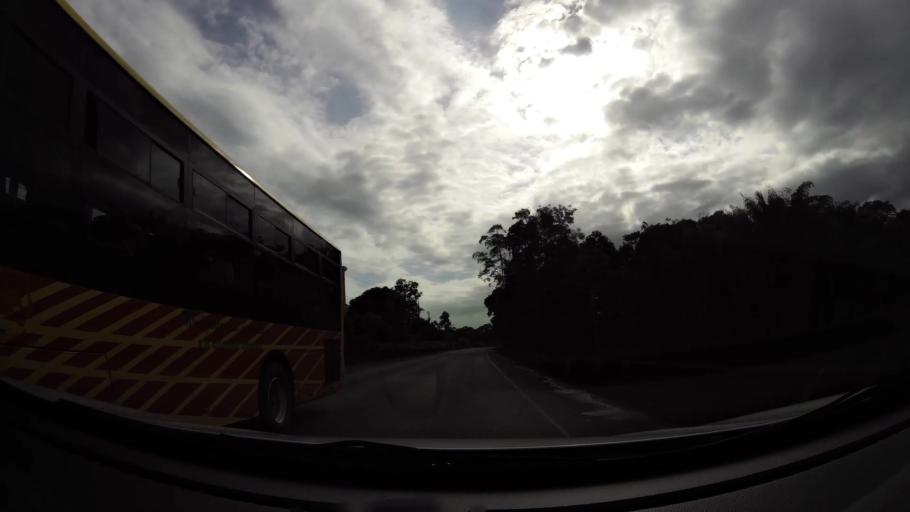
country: CR
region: Limon
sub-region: Canton de Guacimo
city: Guacimo
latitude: 10.1953
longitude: -83.6454
